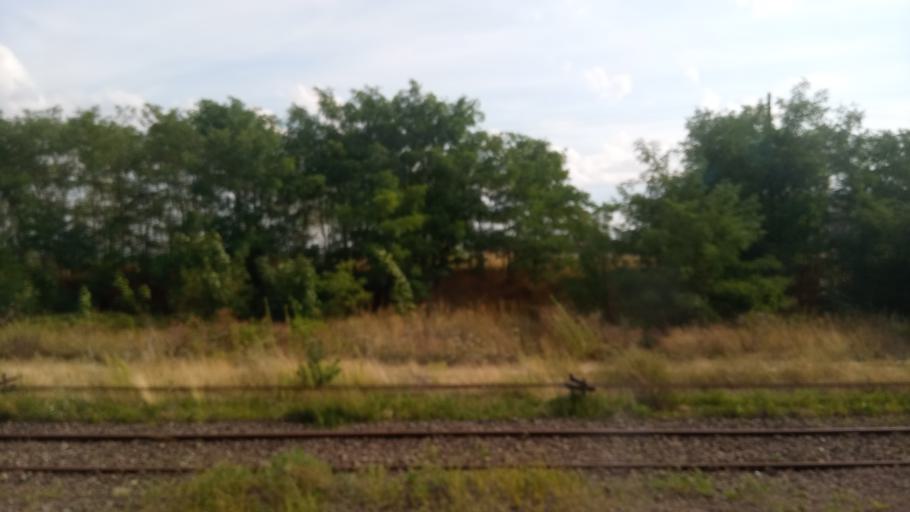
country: PL
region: Greater Poland Voivodeship
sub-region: Powiat pilski
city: Osiek nad Notecia
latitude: 53.1197
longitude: 17.3038
